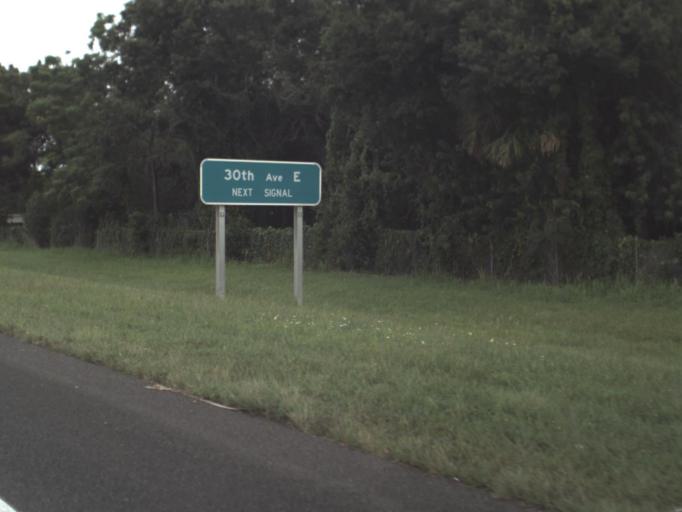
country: US
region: Florida
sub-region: Manatee County
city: Samoset
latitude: 27.4715
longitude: -82.5395
